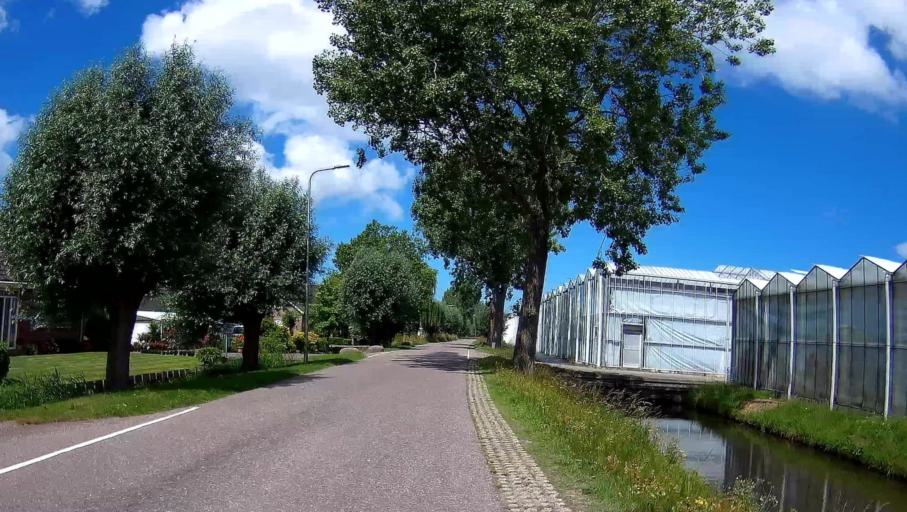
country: NL
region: South Holland
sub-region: Gemeente Westland
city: De Lier
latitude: 51.9877
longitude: 4.2617
